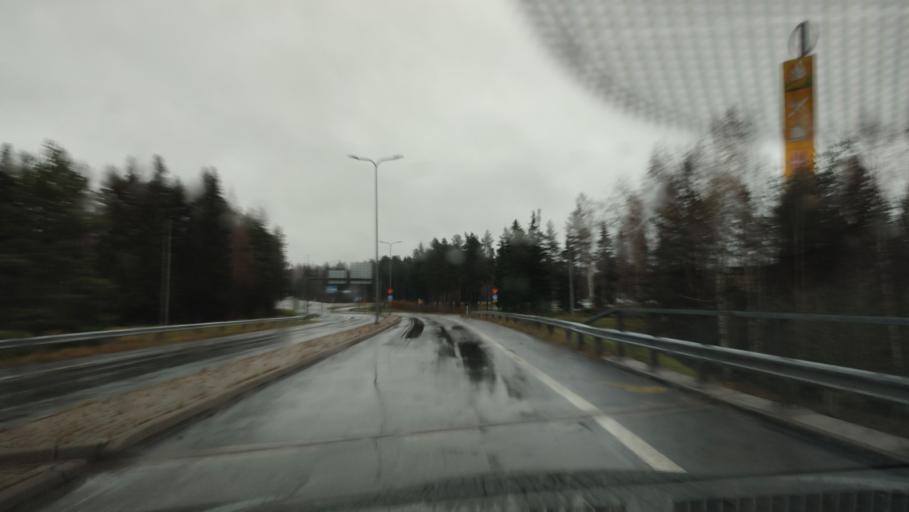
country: FI
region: Ostrobothnia
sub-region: Vaasa
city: Ristinummi
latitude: 63.0539
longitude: 21.7146
